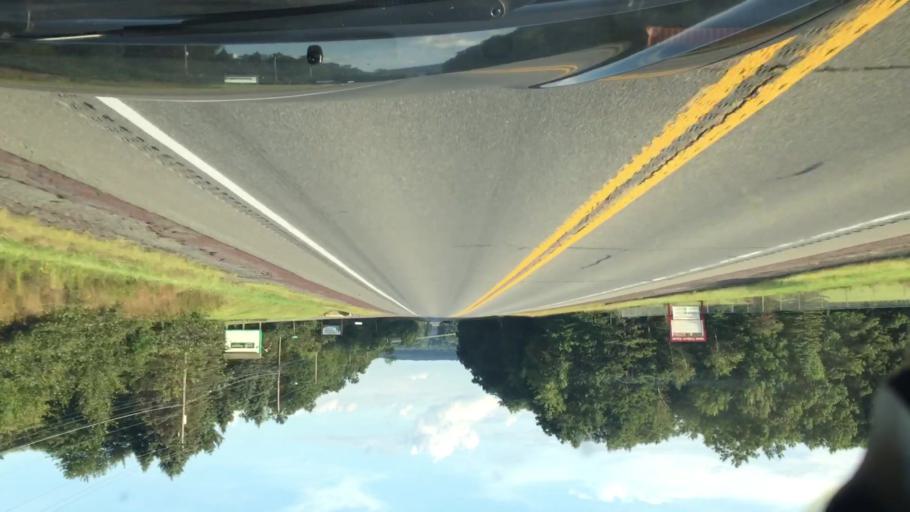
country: US
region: Pennsylvania
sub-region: Carbon County
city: Towamensing Trails
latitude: 40.9509
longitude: -75.6515
